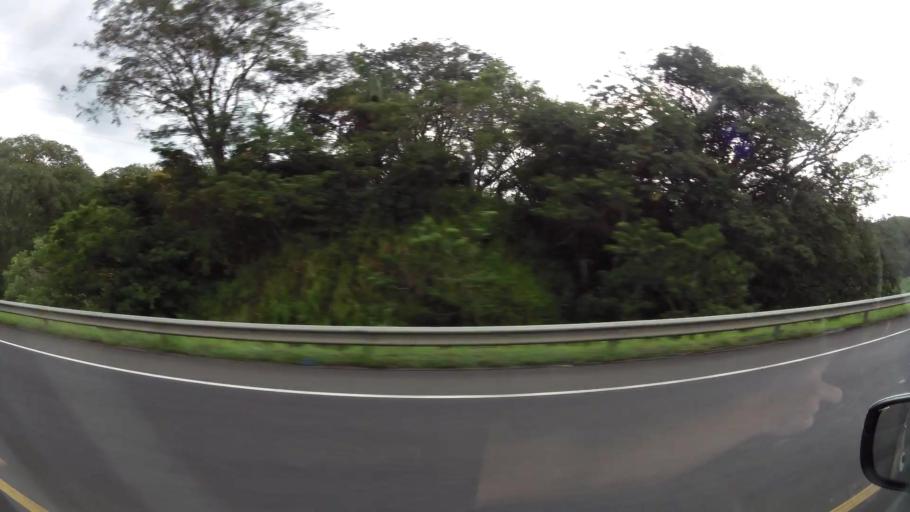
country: CR
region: Alajuela
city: Atenas
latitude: 9.9488
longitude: -84.3629
